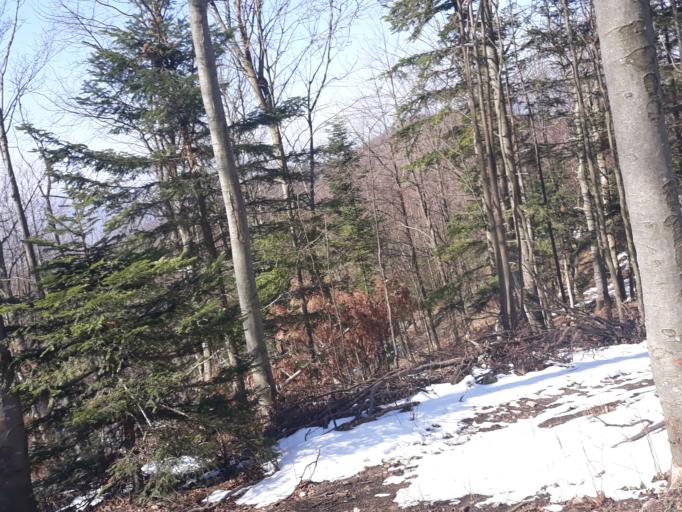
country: HR
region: Varazdinska
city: Ivanec
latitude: 46.1809
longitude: 16.1180
